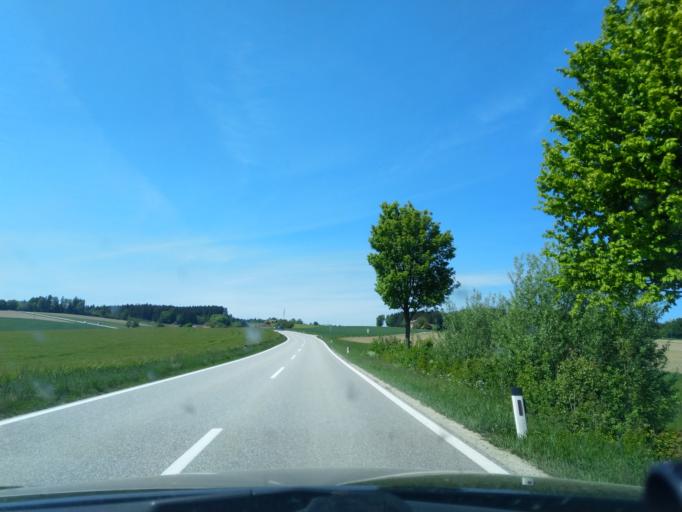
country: AT
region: Upper Austria
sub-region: Politischer Bezirk Ried im Innkreis
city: Ried im Innkreis
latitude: 48.2674
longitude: 13.4127
